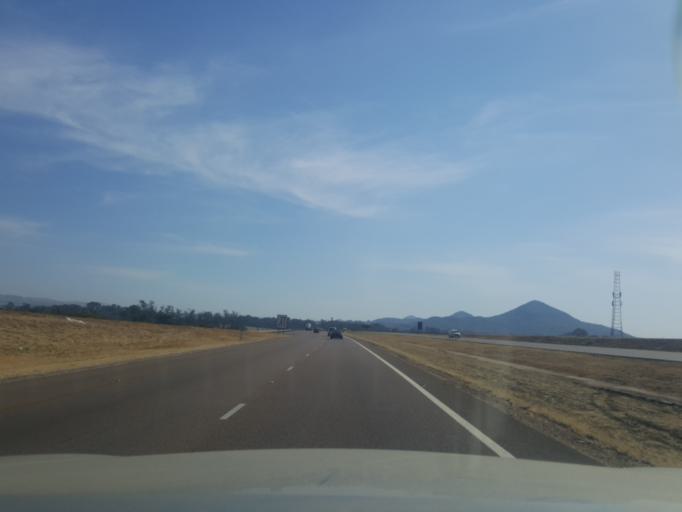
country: ZA
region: Gauteng
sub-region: City of Tshwane Metropolitan Municipality
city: Pretoria
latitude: -25.6382
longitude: 28.2033
